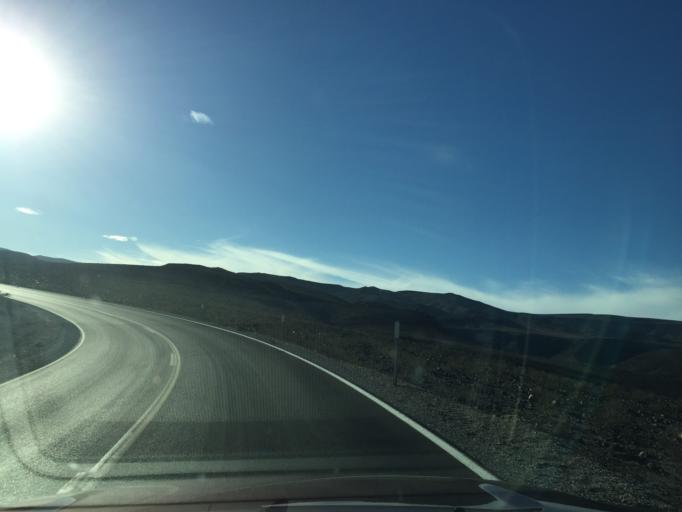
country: US
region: California
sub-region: San Bernardino County
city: Searles Valley
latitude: 36.3420
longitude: -117.5082
